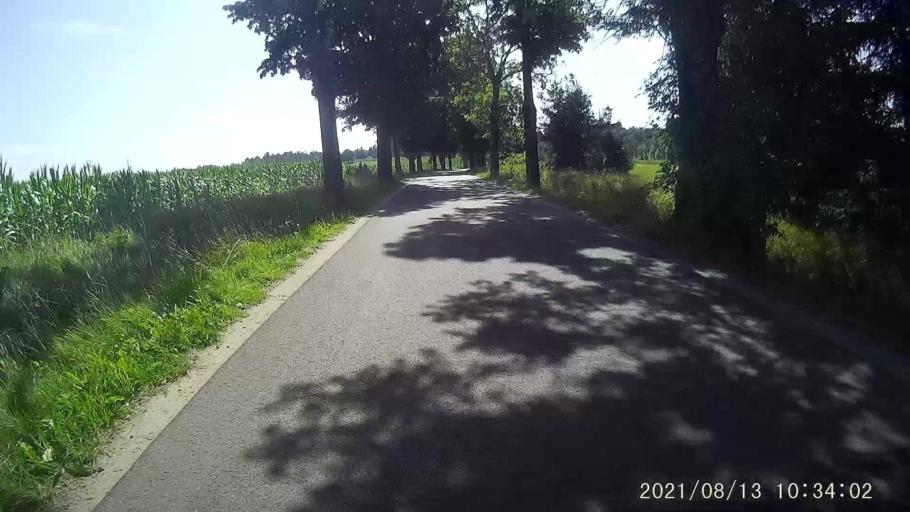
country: PL
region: Lower Silesian Voivodeship
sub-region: Powiat klodzki
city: Duszniki-Zdroj
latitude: 50.4245
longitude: 16.3756
